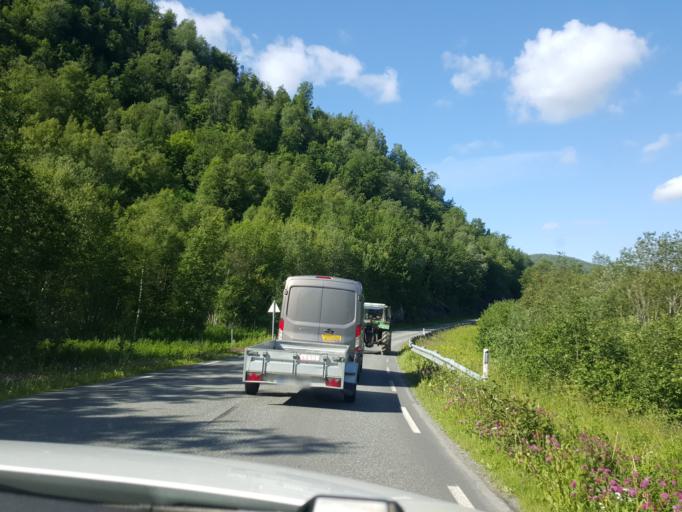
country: NO
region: Nordland
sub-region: Bodo
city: Loding
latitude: 67.1103
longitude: 15.0143
